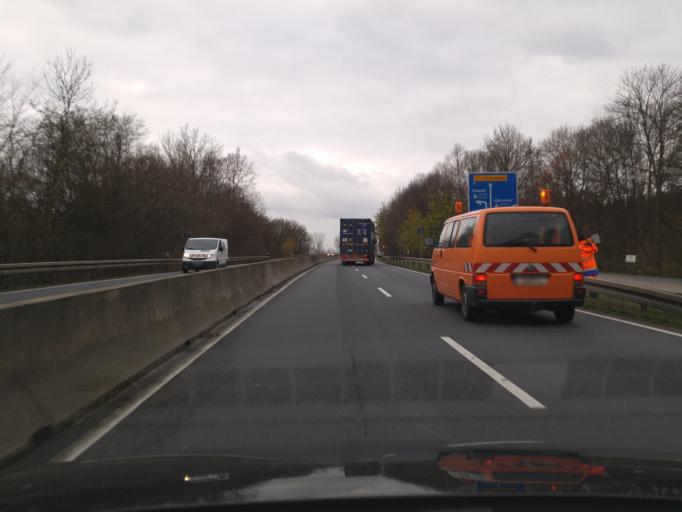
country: DE
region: Lower Saxony
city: Holle
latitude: 52.1055
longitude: 10.1521
